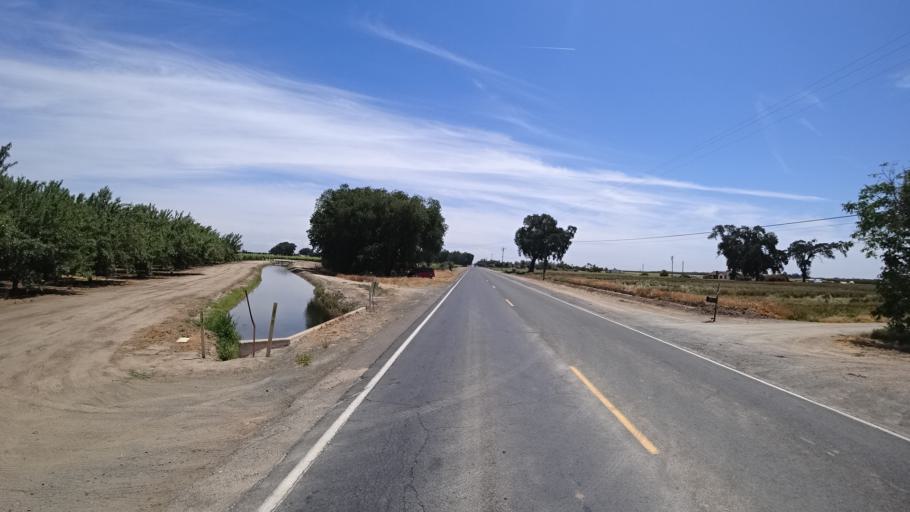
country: US
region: California
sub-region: Kings County
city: Lemoore
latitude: 36.3425
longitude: -119.8028
